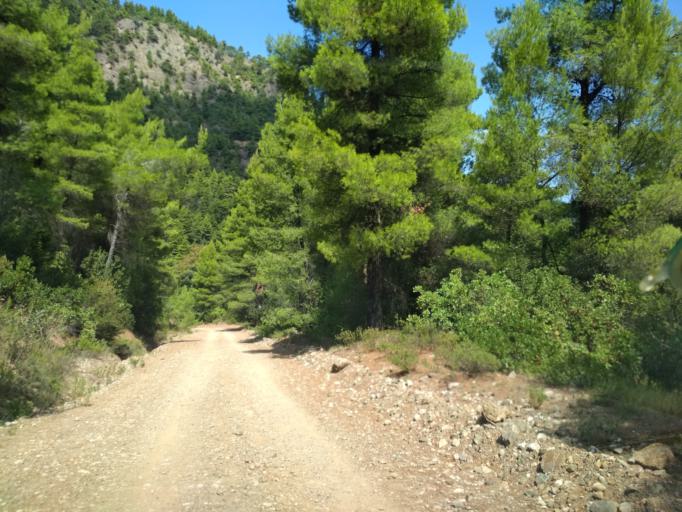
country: GR
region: Central Greece
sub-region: Nomos Evvoias
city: Roviai
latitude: 38.8423
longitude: 23.2794
